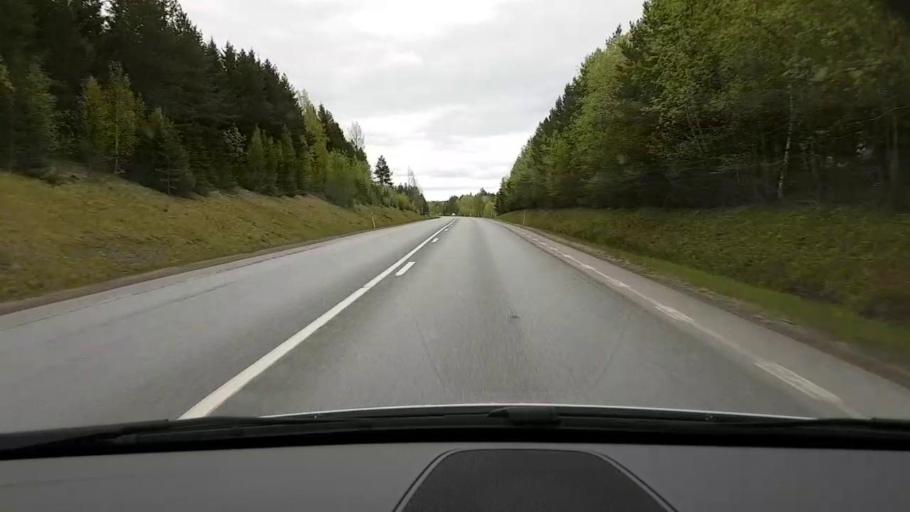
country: SE
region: Jaemtland
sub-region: Krokoms Kommun
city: Valla
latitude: 63.3267
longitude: 14.0442
